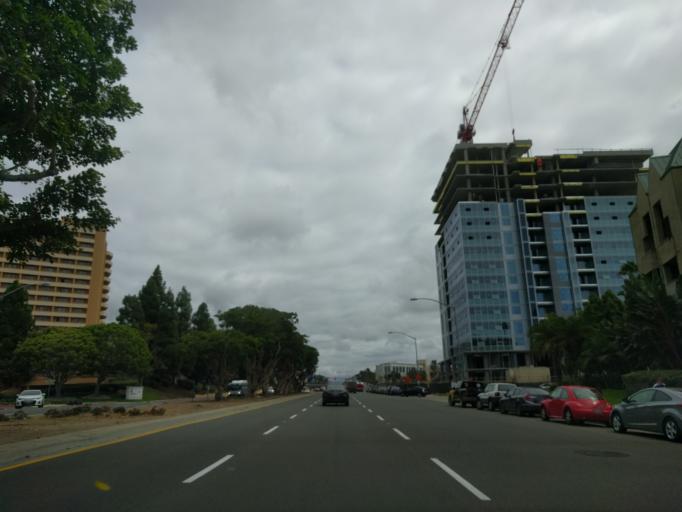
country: US
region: California
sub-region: San Diego County
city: La Jolla
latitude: 32.8719
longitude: -117.2169
